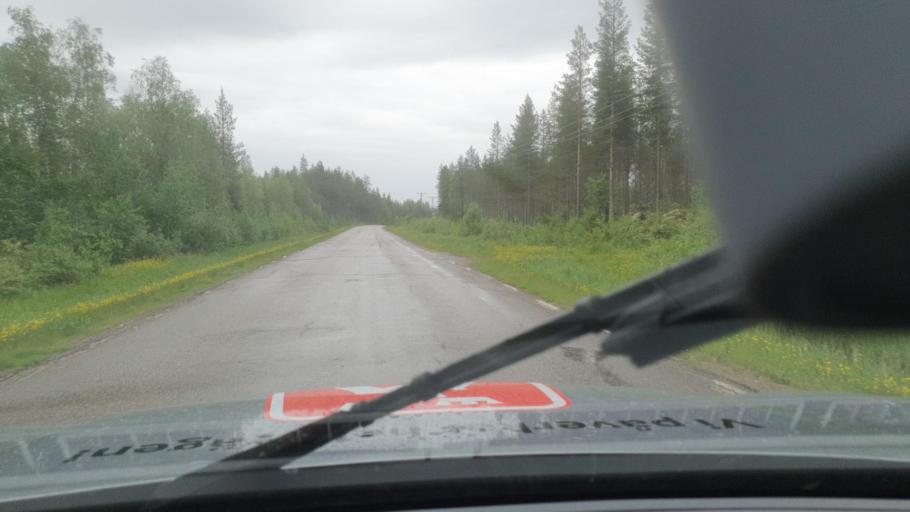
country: SE
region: Norrbotten
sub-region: Pajala Kommun
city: Pajala
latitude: 66.8124
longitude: 23.1194
